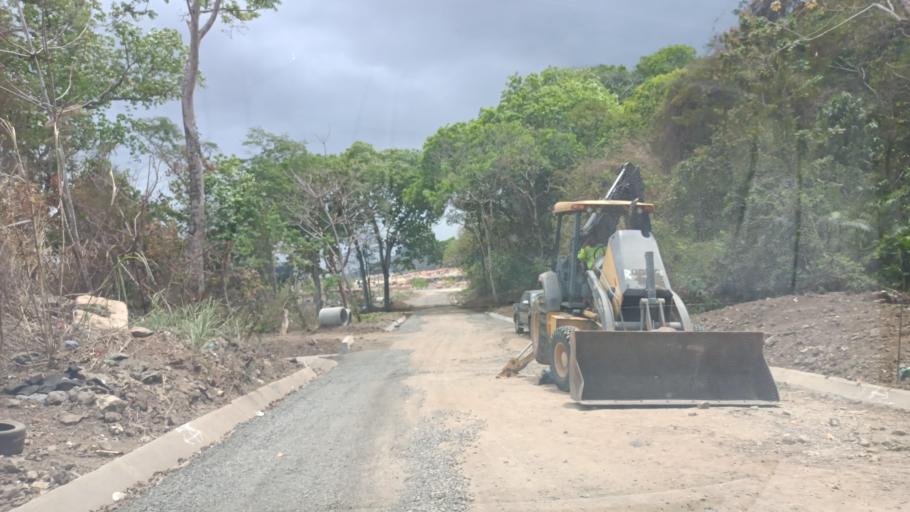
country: PA
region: Panama
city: Las Cumbres
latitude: 9.0657
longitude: -79.5680
